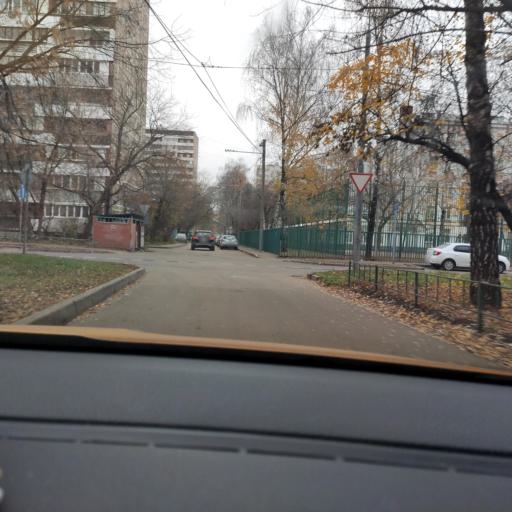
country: RU
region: Moscow
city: Sviblovo
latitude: 55.8513
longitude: 37.6344
